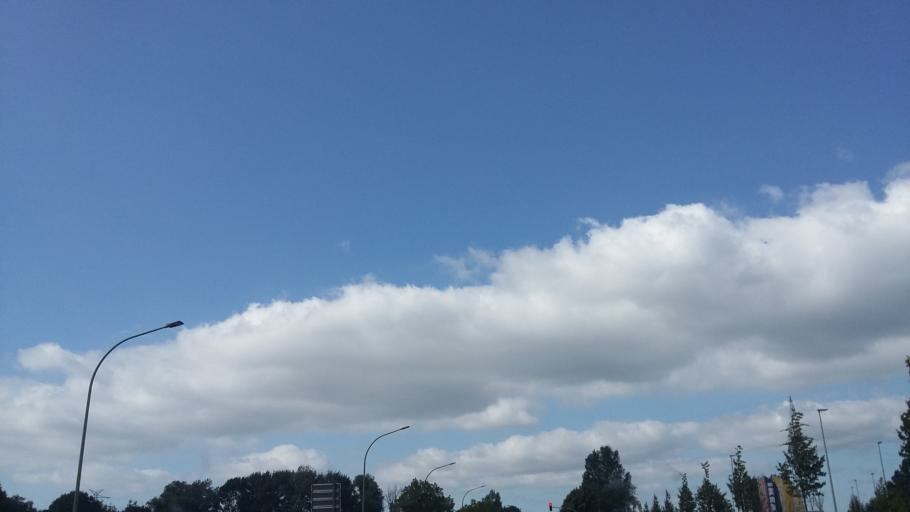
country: DE
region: Lower Saxony
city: Loxstedt
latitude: 53.4882
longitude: 8.6030
